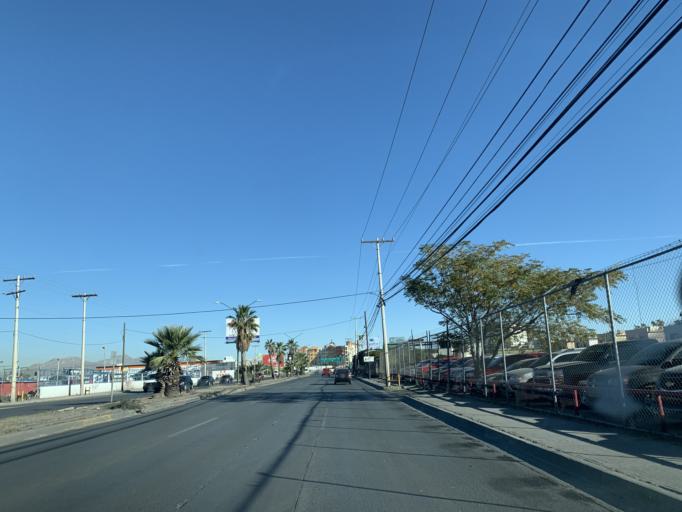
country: MX
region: Chihuahua
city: Ciudad Juarez
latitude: 31.6786
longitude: -106.4085
